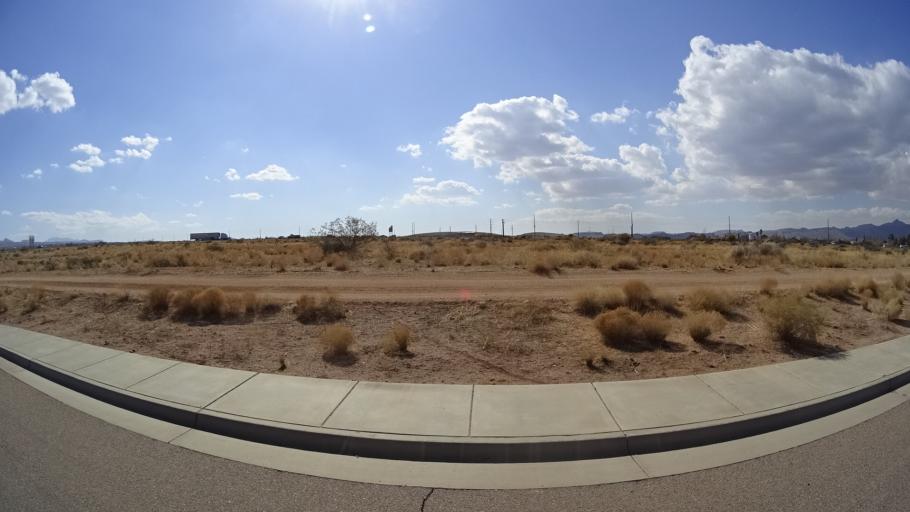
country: US
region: Arizona
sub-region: Mohave County
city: New Kingman-Butler
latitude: 35.2185
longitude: -113.9901
